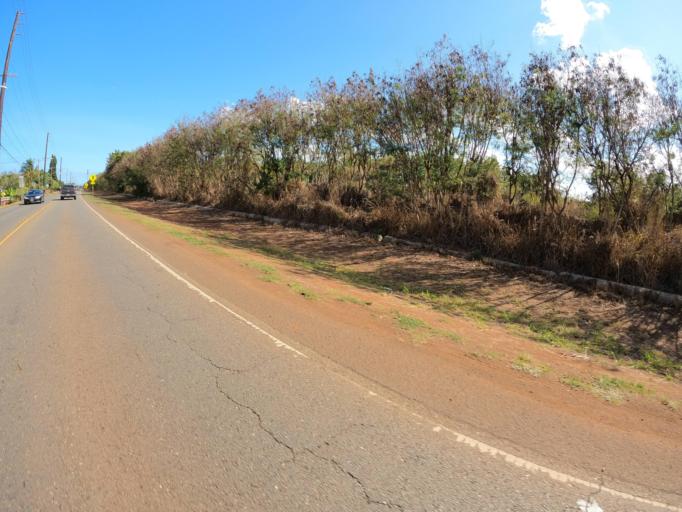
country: US
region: Hawaii
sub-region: Honolulu County
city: Hale'iwa
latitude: 21.5694
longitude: -158.1090
